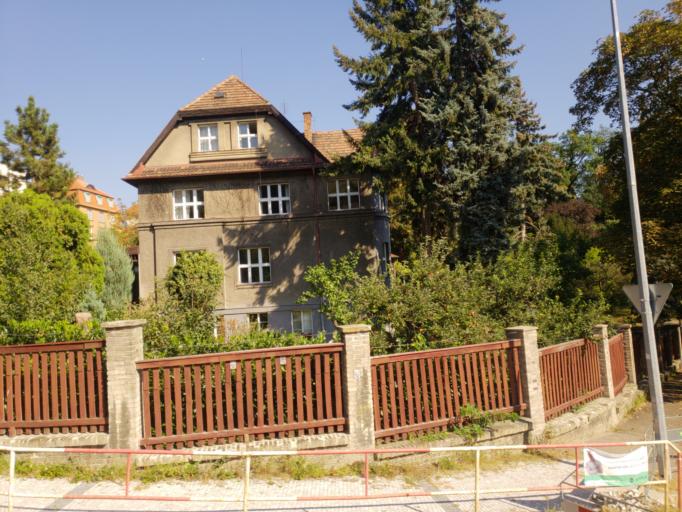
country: CZ
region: Praha
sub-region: Praha 1
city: Mala Strana
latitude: 50.0742
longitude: 14.3893
